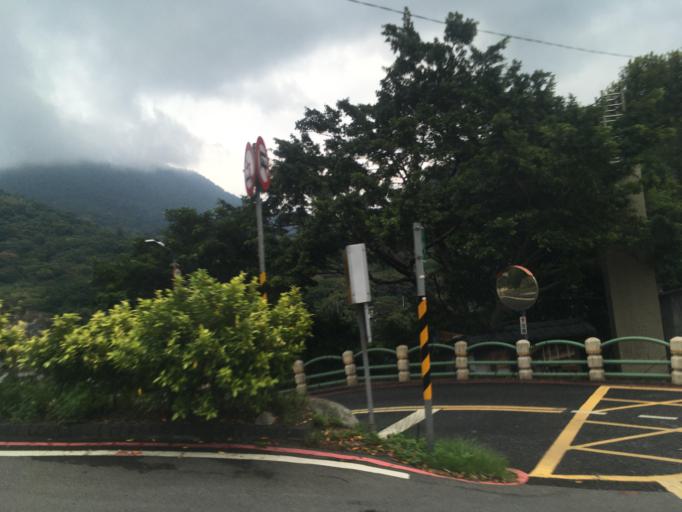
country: TW
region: Taipei
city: Taipei
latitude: 25.1384
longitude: 121.5282
